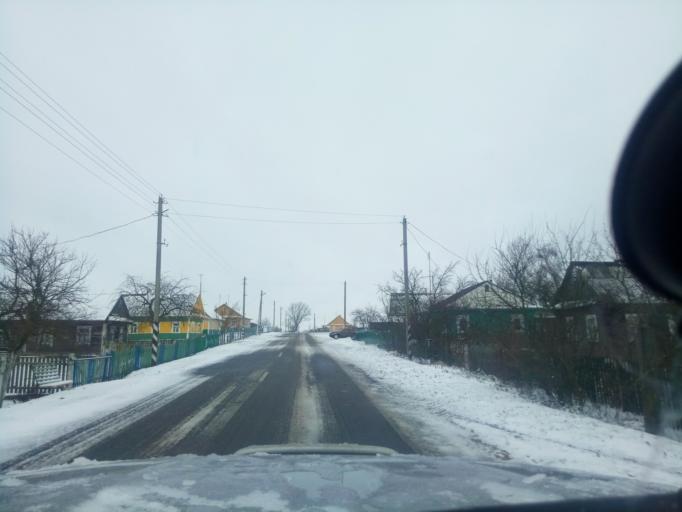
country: BY
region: Minsk
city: Klyetsk
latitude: 53.0095
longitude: 26.7021
